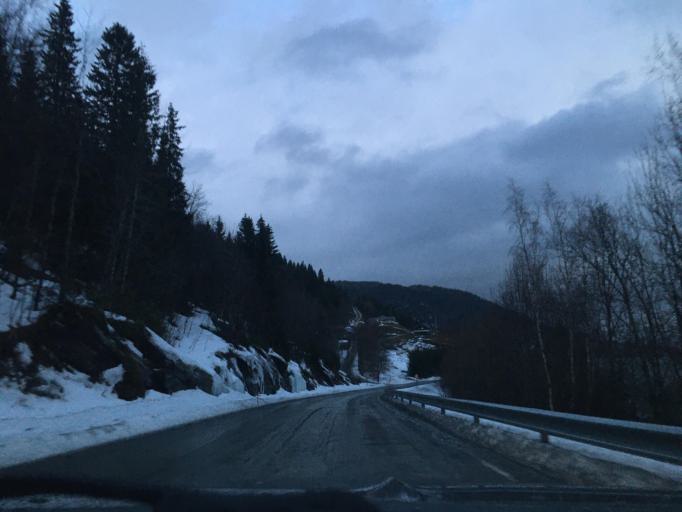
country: NO
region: Nordland
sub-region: Rana
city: Hauknes
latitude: 66.3070
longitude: 13.9730
